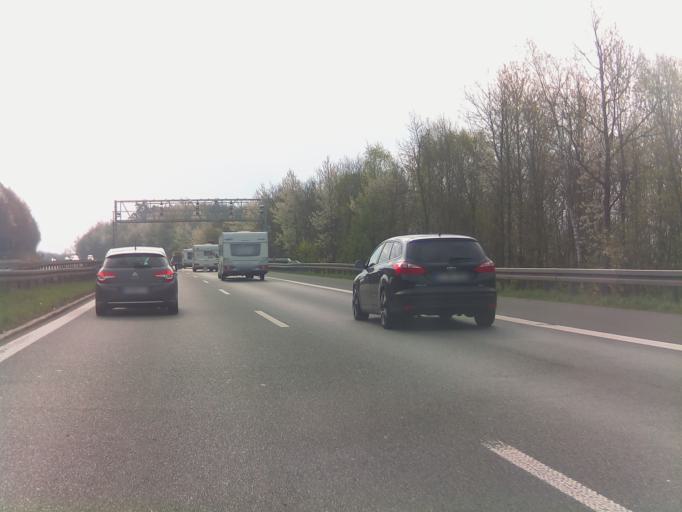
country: DE
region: Bavaria
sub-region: Regierungsbezirk Mittelfranken
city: Schnelldorf
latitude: 49.2075
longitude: 10.1875
